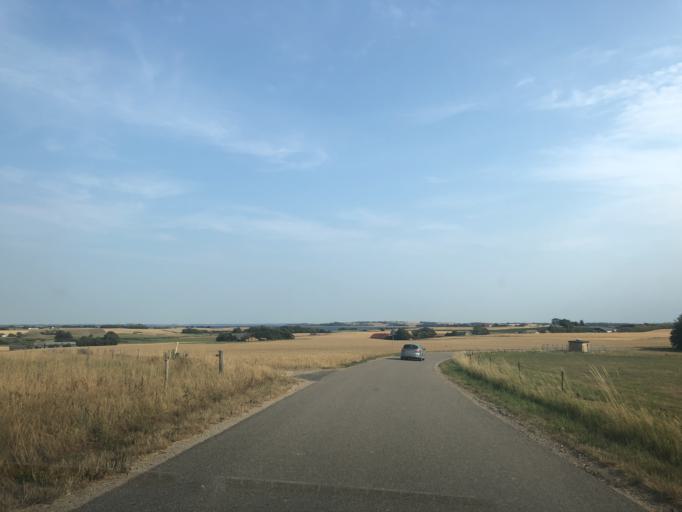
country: DK
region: North Denmark
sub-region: Morso Kommune
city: Nykobing Mors
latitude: 56.8309
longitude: 9.0171
